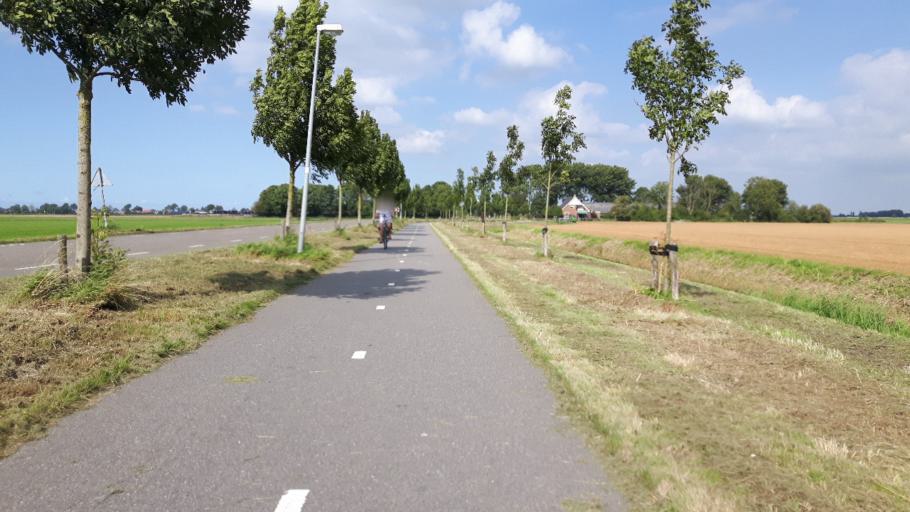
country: NL
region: North Holland
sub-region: Gemeente Medemblik
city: Opperdoes
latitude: 52.7122
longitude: 5.0917
